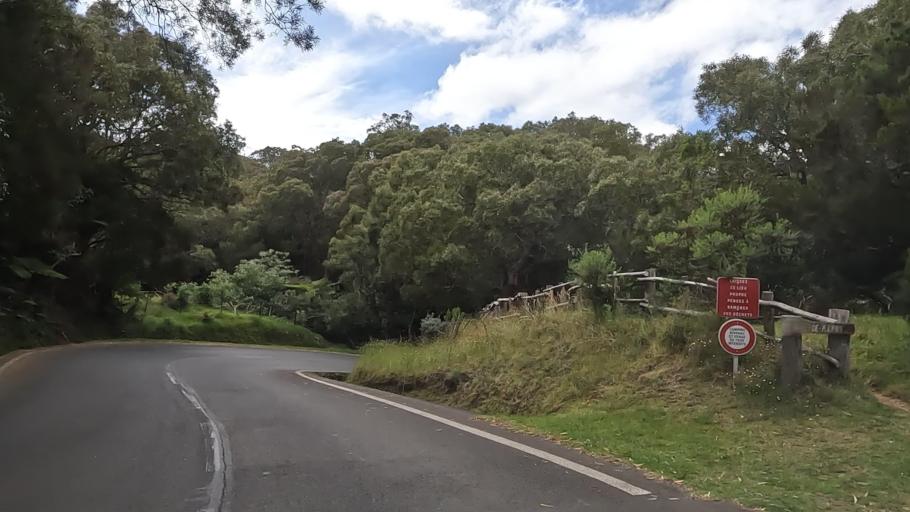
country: RE
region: Reunion
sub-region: Reunion
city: Le Tampon
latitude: -21.2408
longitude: 55.5861
